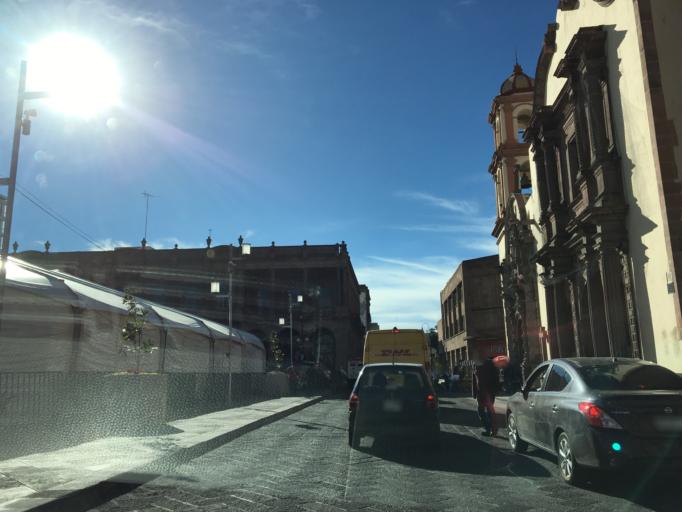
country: MX
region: San Luis Potosi
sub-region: San Luis Potosi
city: San Luis Potosi
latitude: 22.1524
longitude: -100.9781
